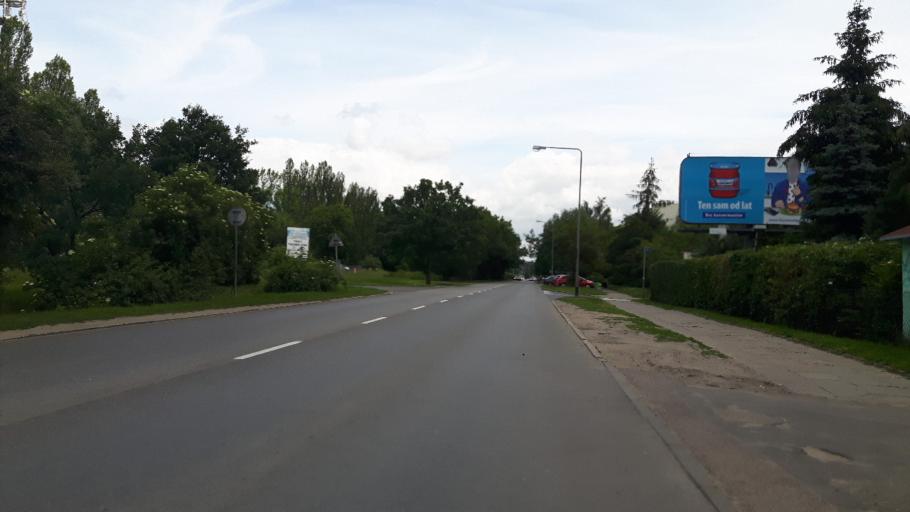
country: PL
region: West Pomeranian Voivodeship
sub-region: Powiat policki
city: Przeclaw
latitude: 53.3993
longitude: 14.4958
